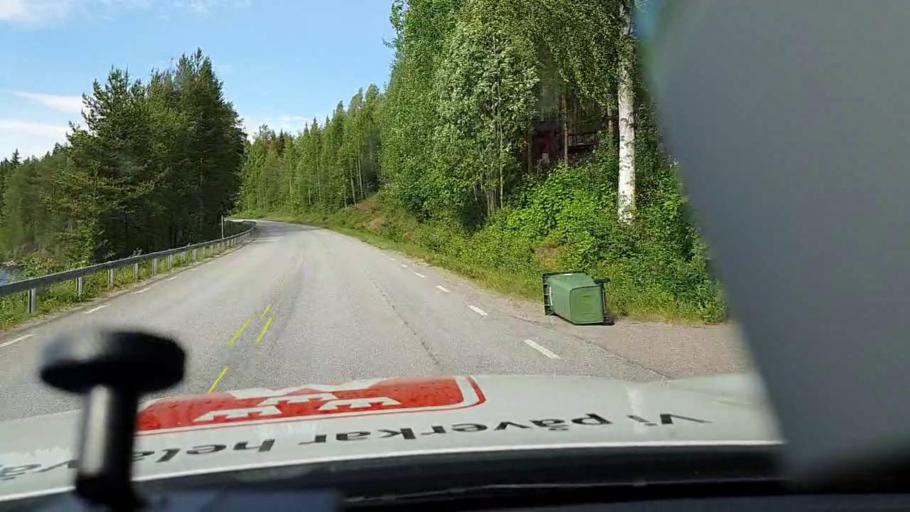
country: SE
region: Norrbotten
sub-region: Gallivare Kommun
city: Gaellivare
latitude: 66.4523
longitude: 20.6567
